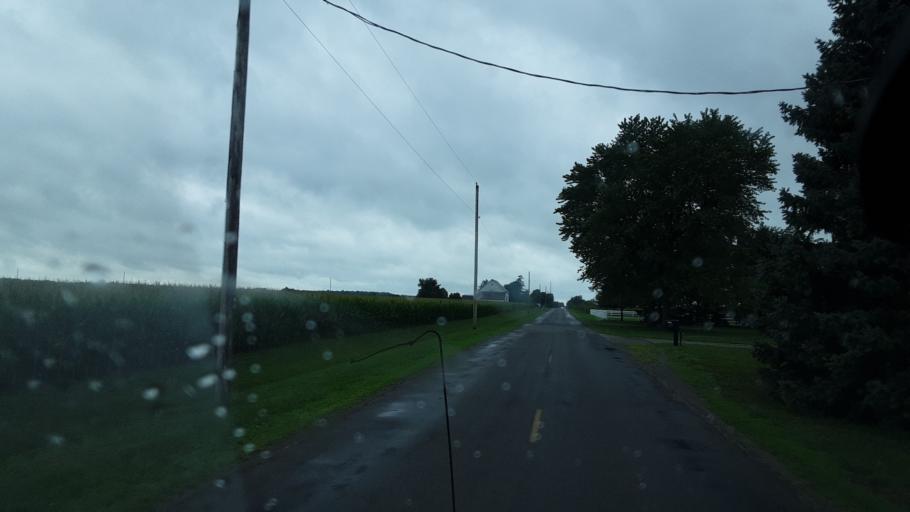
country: US
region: Ohio
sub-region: Van Wert County
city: Van Wert
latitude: 40.8003
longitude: -84.6416
